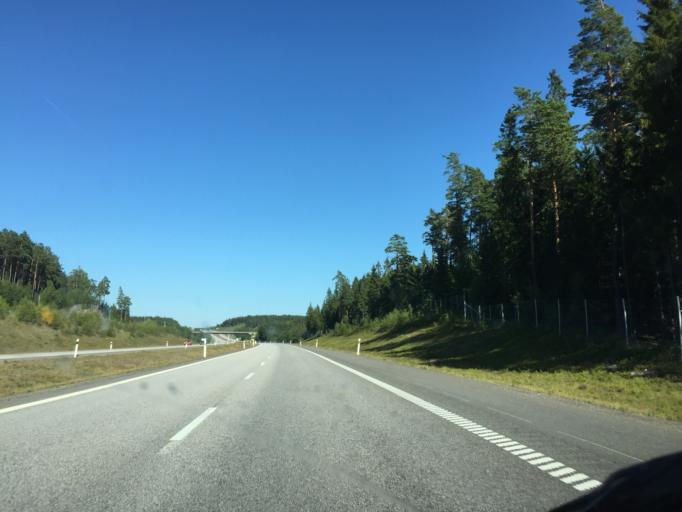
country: SE
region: OErebro
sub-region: Lindesbergs Kommun
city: Fellingsbro
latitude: 59.3783
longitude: 15.6434
